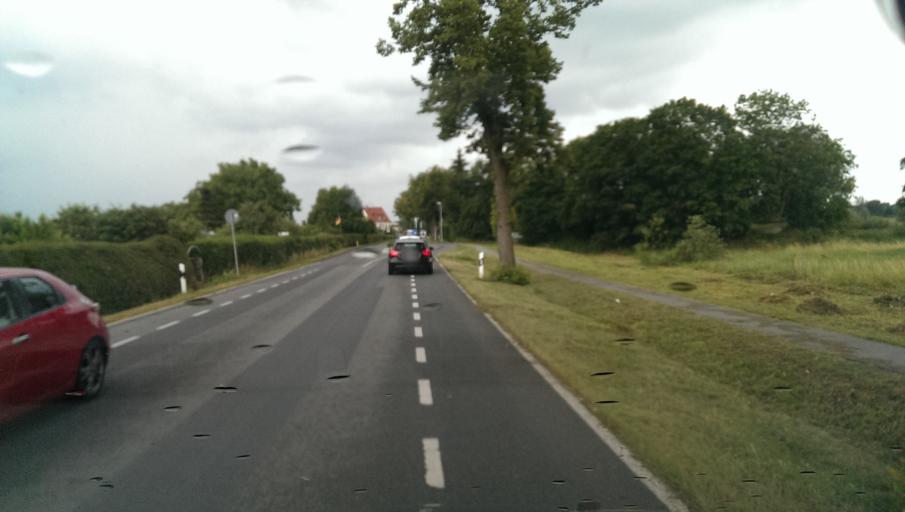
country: DE
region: Brandenburg
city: Rathenow
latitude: 52.6188
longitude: 12.3316
